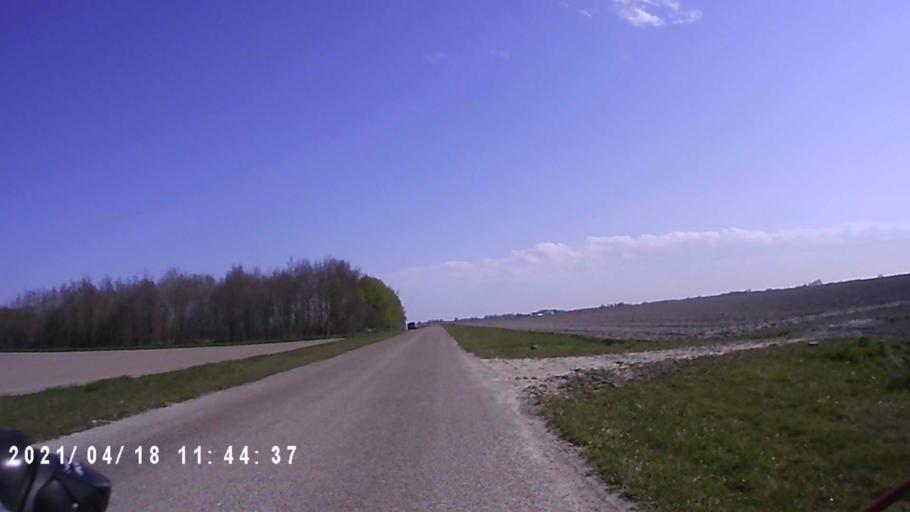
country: NL
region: Groningen
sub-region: Gemeente Zuidhorn
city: Grijpskerk
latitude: 53.3205
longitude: 6.2581
